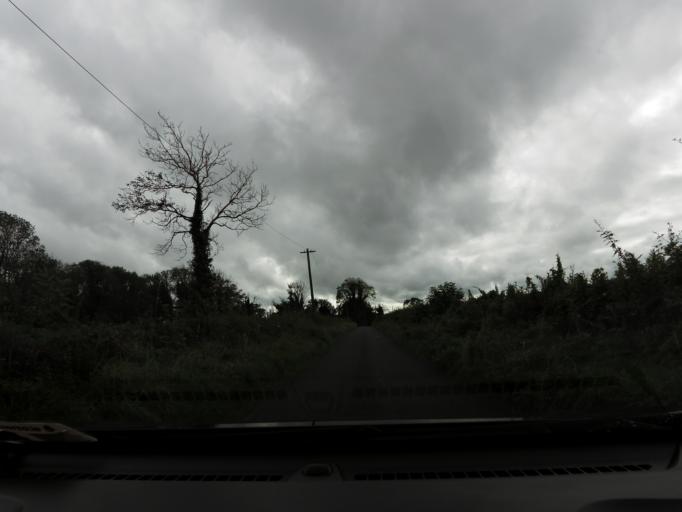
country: IE
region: Connaught
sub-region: County Galway
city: Loughrea
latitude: 53.2934
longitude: -8.5902
